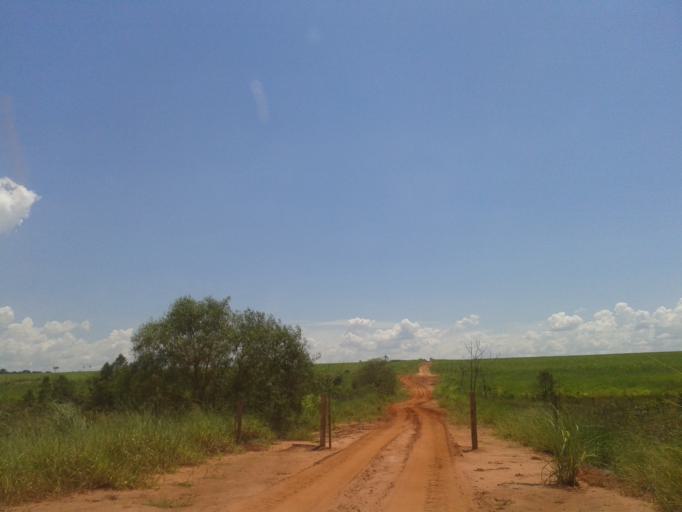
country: BR
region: Minas Gerais
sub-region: Santa Vitoria
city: Santa Vitoria
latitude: -19.1731
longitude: -50.4348
